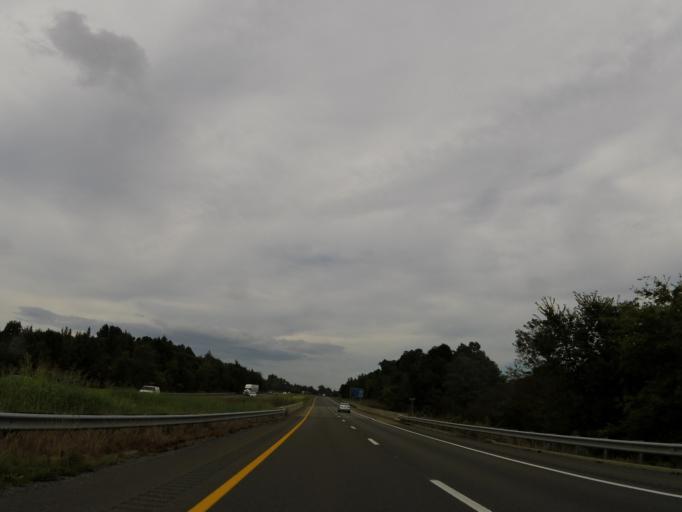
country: US
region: Kentucky
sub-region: Lyon County
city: Eddyville
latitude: 37.0718
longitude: -88.1421
